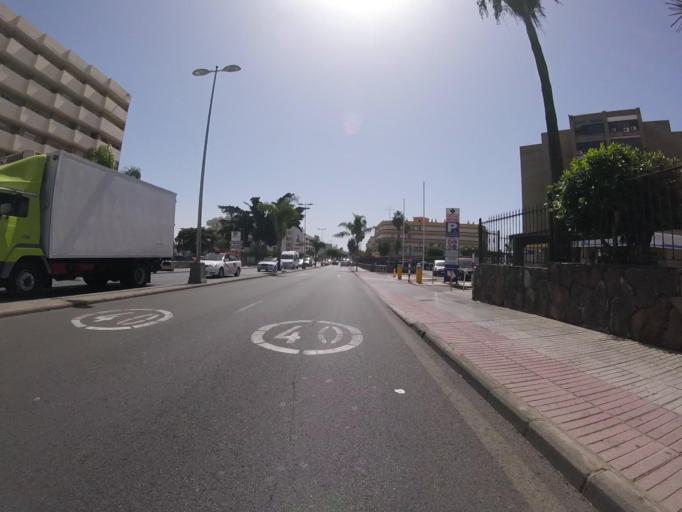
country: ES
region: Canary Islands
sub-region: Provincia de Las Palmas
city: Playa del Ingles
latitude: 27.7631
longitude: -15.5790
